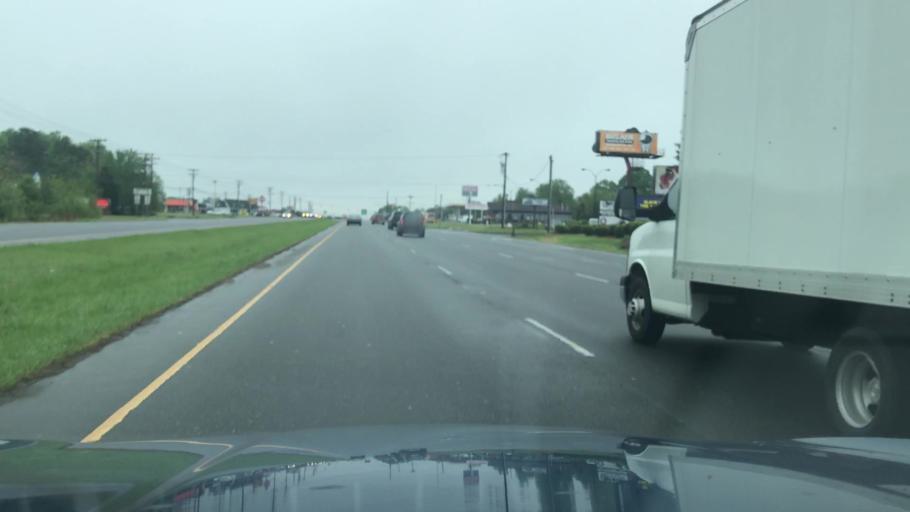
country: US
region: North Carolina
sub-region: Mecklenburg County
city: Matthews
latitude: 35.1217
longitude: -80.7010
